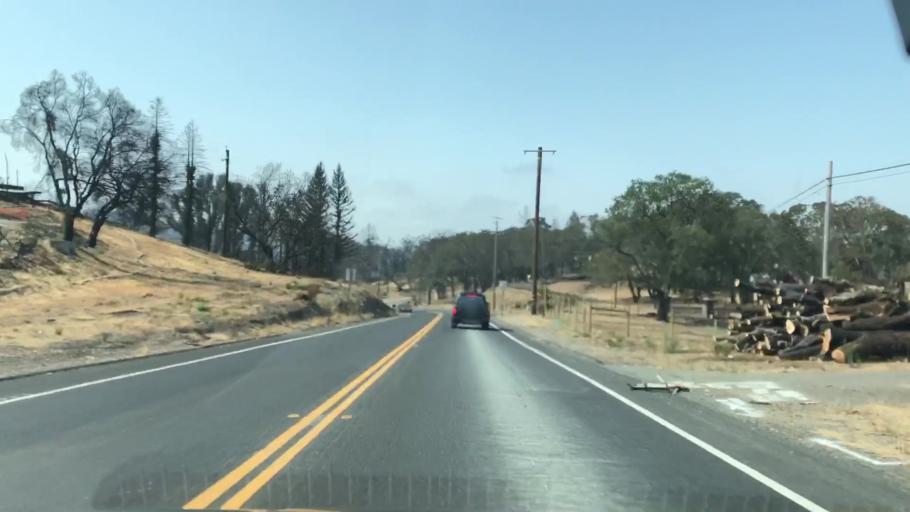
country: US
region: California
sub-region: Sonoma County
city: Larkfield-Wikiup
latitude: 38.5191
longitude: -122.7199
